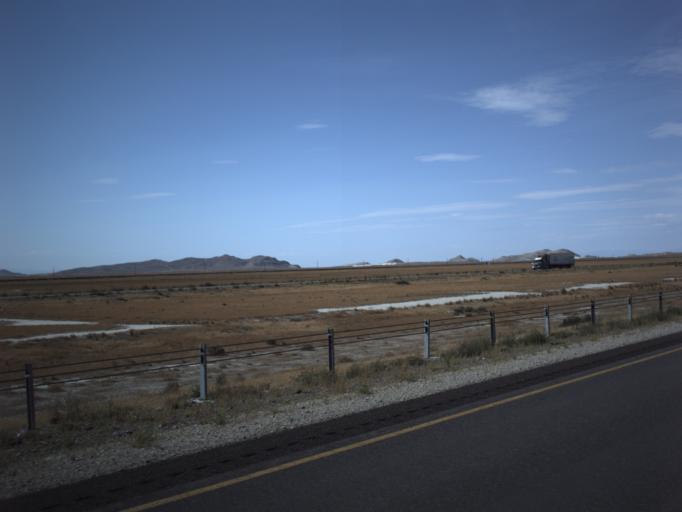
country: US
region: Utah
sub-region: Tooele County
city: Grantsville
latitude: 40.7269
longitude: -113.2198
